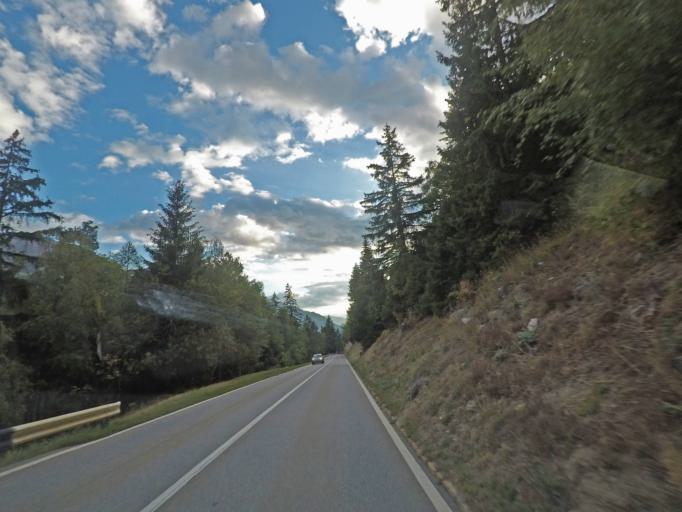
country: CH
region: Valais
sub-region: Goms District
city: Fiesch
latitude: 46.4054
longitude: 8.1442
